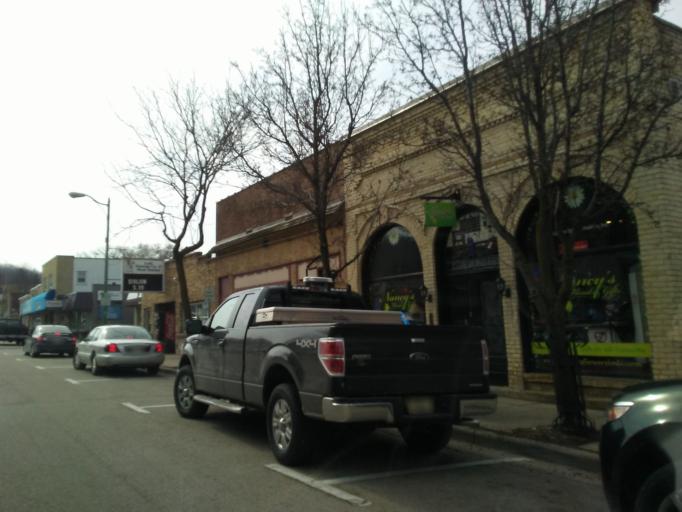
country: US
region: Wisconsin
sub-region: Columbia County
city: Lodi
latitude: 43.3130
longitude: -89.5260
